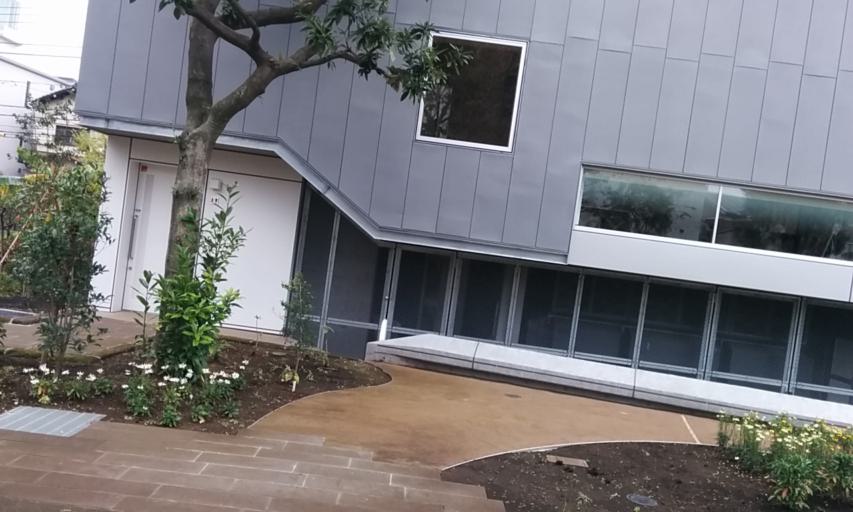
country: JP
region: Tokyo
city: Tokyo
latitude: 35.7040
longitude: 139.7256
